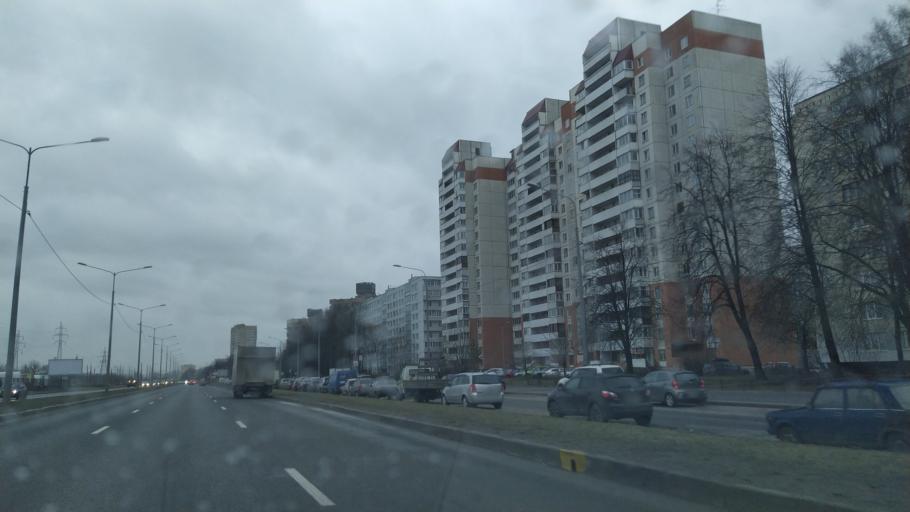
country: RU
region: Leningrad
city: Akademicheskoe
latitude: 60.0240
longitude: 30.3987
